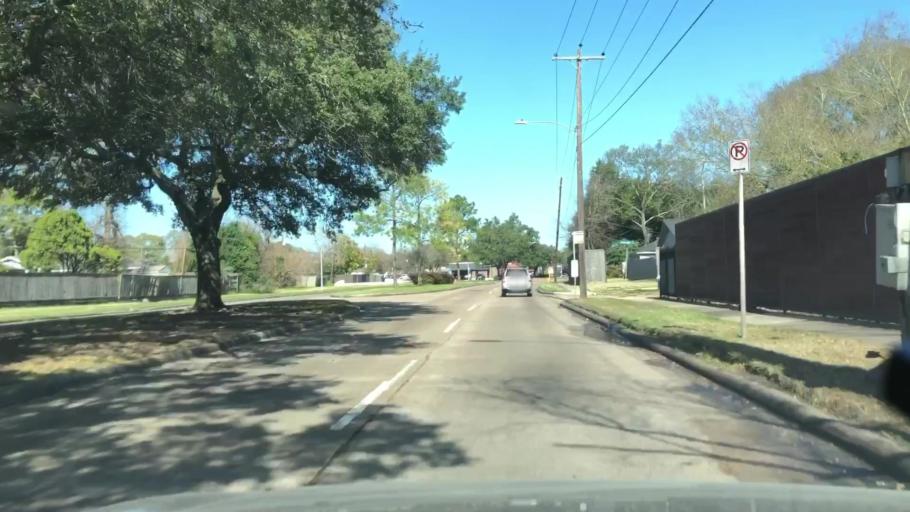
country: US
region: Texas
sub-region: Harris County
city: Bellaire
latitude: 29.6839
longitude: -95.4928
